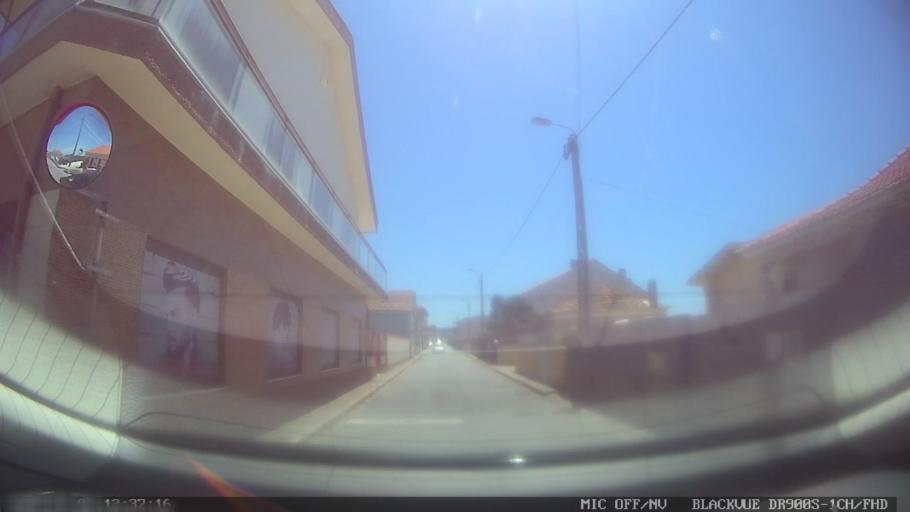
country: PT
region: Porto
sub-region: Matosinhos
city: Lavra
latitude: 41.2559
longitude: -8.7187
